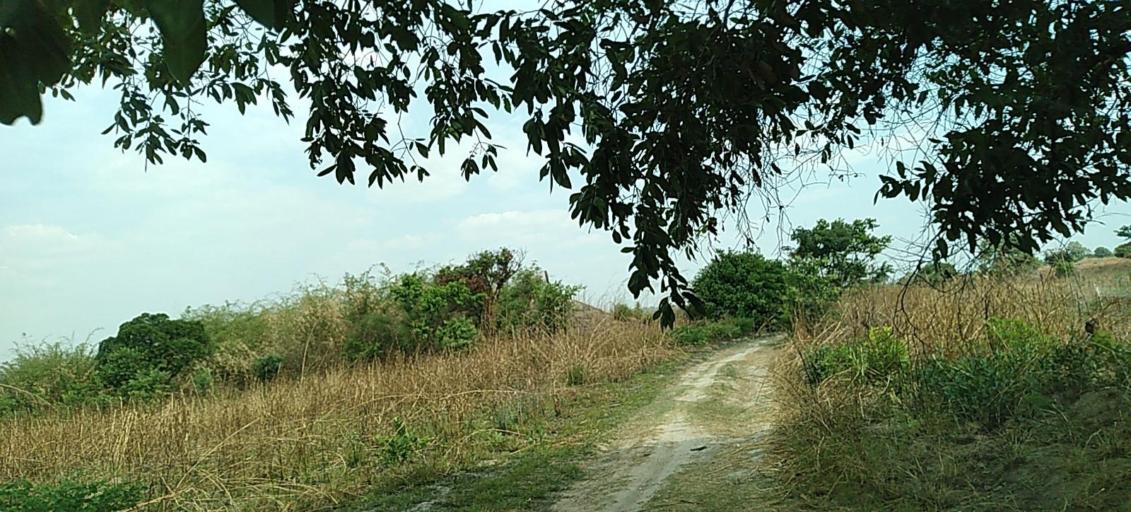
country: ZM
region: Copperbelt
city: Chililabombwe
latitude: -12.3466
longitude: 27.7926
